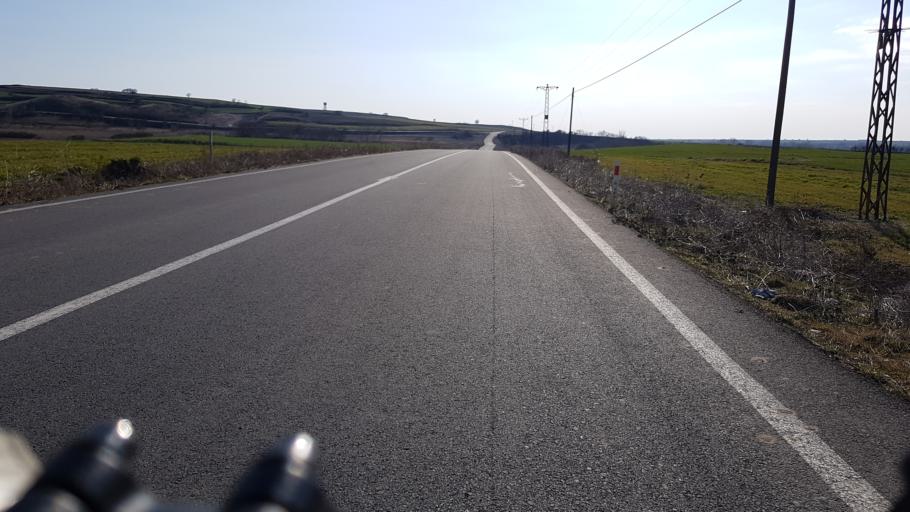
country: TR
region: Tekirdag
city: Saray
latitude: 41.3611
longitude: 27.8547
